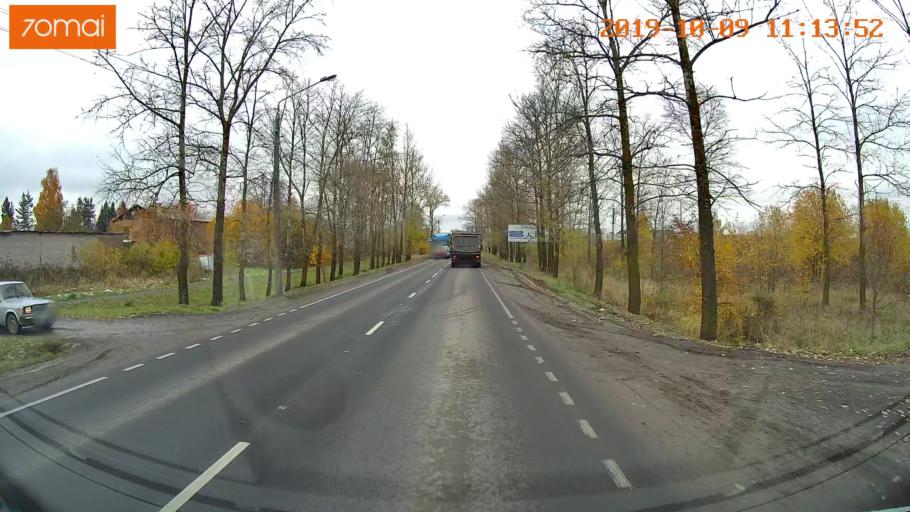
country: RU
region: Vologda
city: Vologda
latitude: 59.1847
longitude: 39.8477
